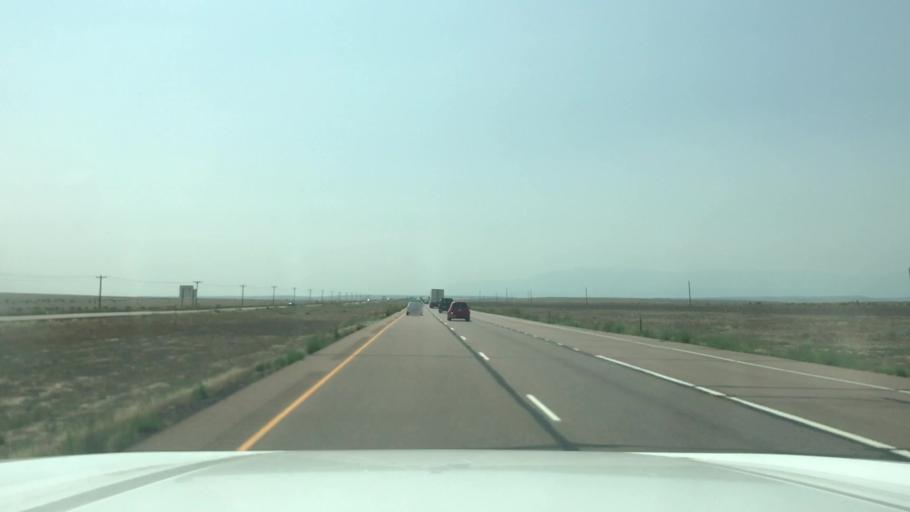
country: US
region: Colorado
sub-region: Pueblo County
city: Pueblo
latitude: 38.1592
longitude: -104.6454
